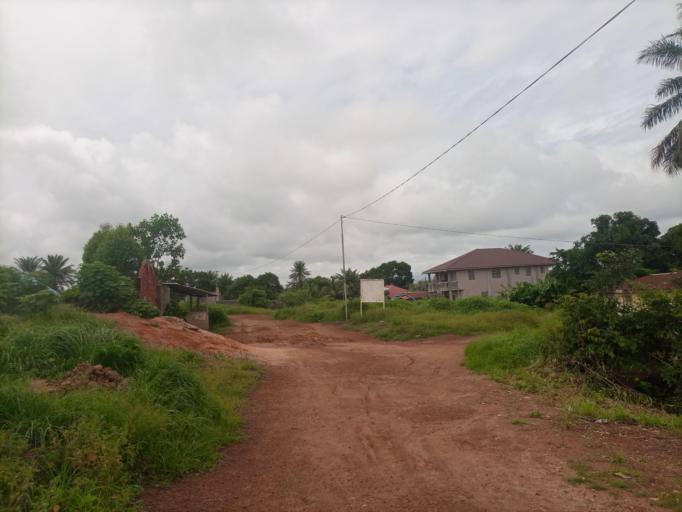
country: SL
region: Northern Province
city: Masoyila
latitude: 8.5945
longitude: -13.1777
